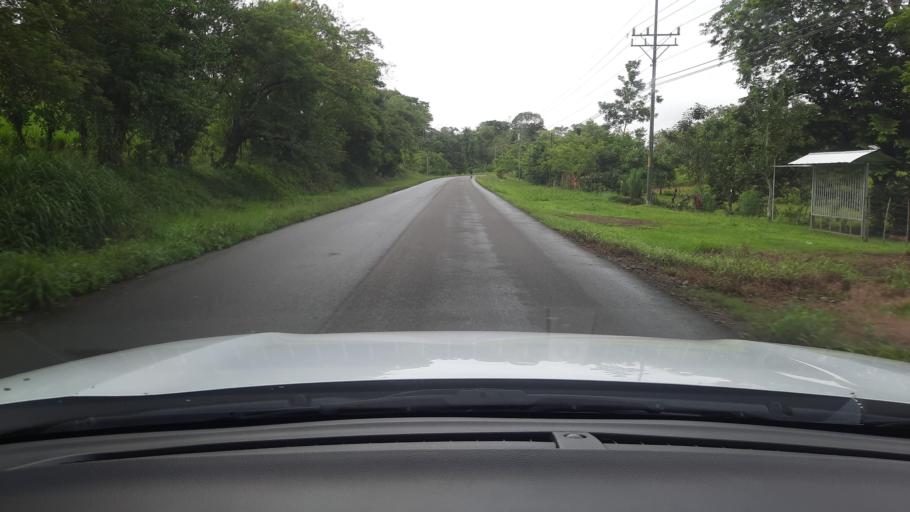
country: CR
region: Alajuela
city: San Jose
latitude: 10.9490
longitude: -85.1217
